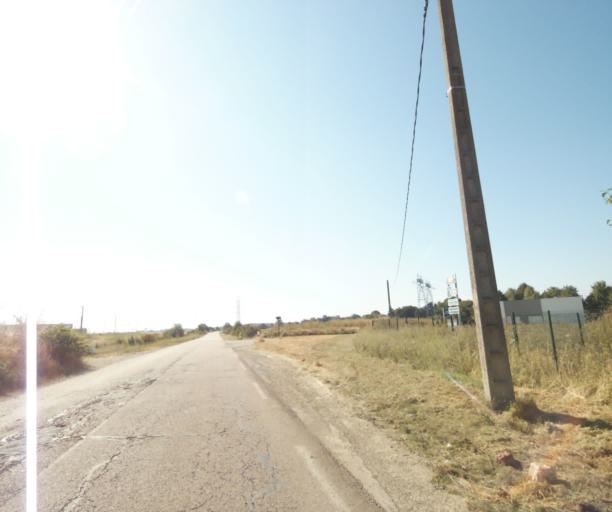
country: FR
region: Ile-de-France
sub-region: Departement de Seine-et-Marne
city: Moissy-Cramayel
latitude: 48.6105
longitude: 2.5857
